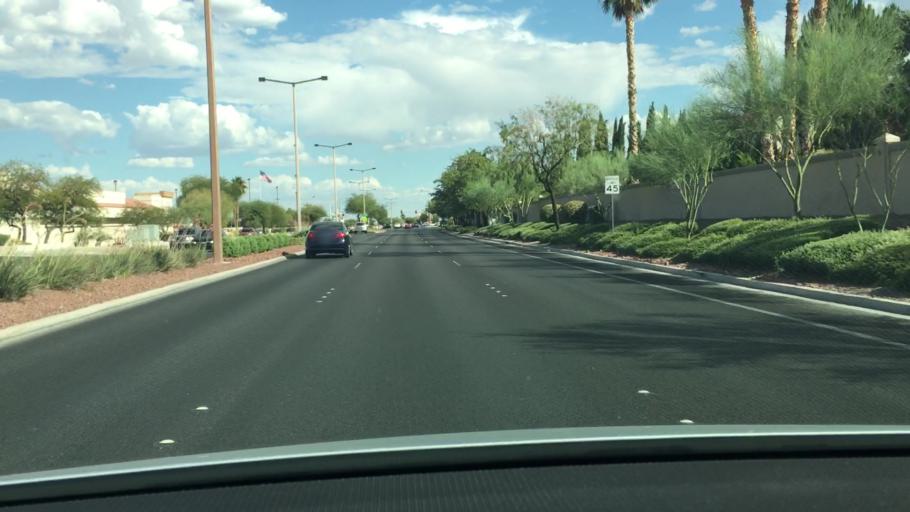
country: US
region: Nevada
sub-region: Clark County
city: Summerlin South
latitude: 36.2017
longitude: -115.2854
